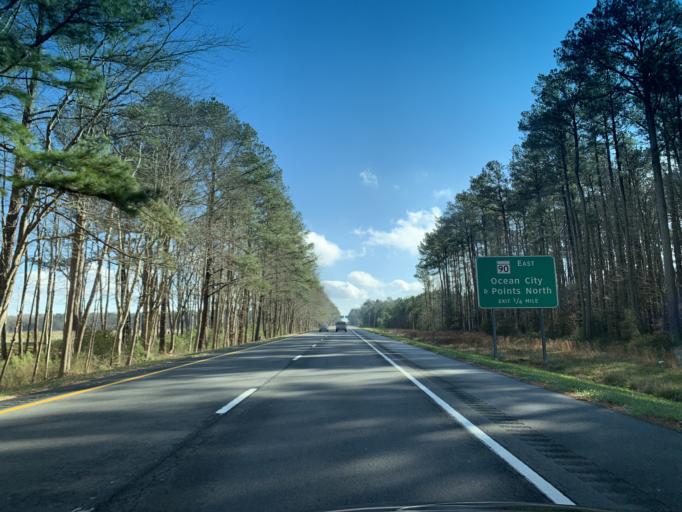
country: US
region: Maryland
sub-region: Worcester County
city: Berlin
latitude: 38.3749
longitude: -75.2823
